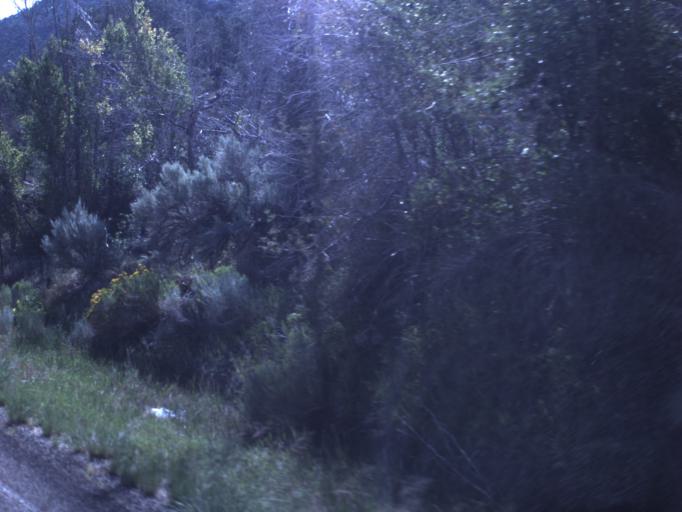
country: US
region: Utah
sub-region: Duchesne County
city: Duchesne
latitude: 40.2965
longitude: -110.5474
